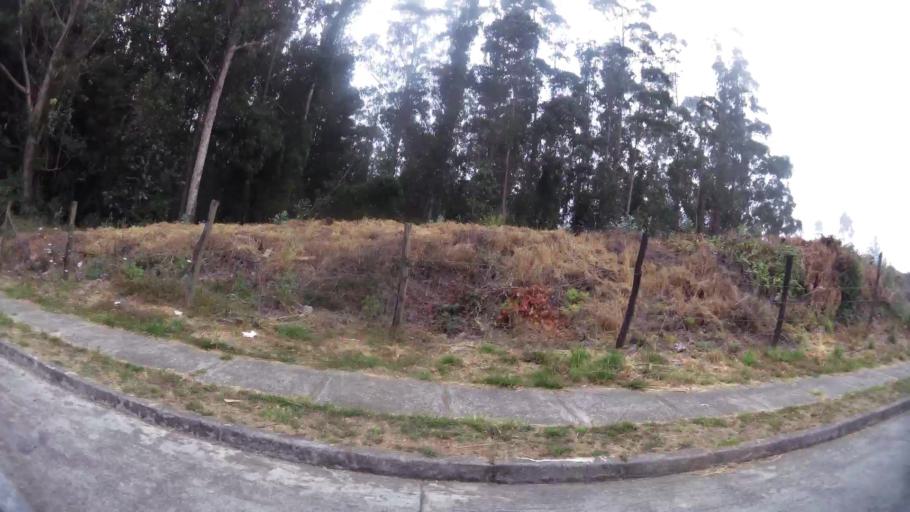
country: CL
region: Biobio
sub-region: Provincia de Concepcion
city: Concepcion
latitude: -36.8262
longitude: -73.0278
